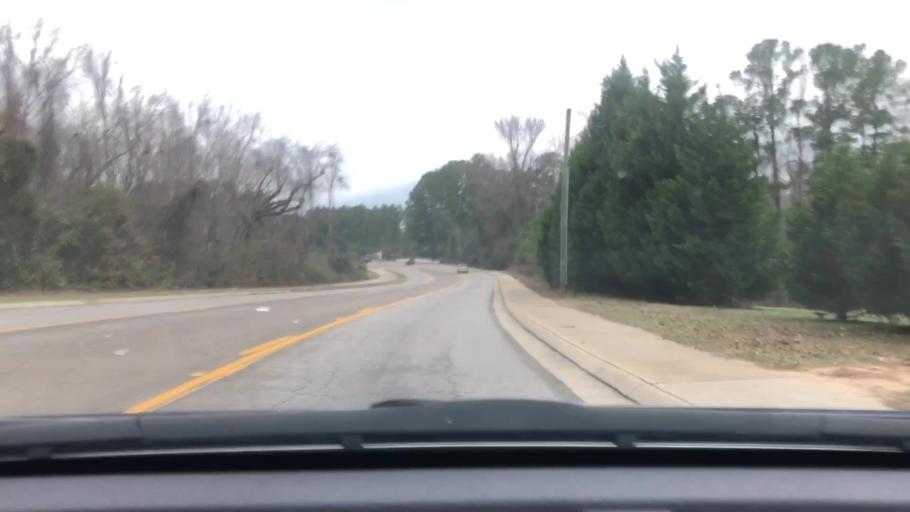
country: US
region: South Carolina
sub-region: Sumter County
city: South Sumter
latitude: 33.9177
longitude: -80.3916
